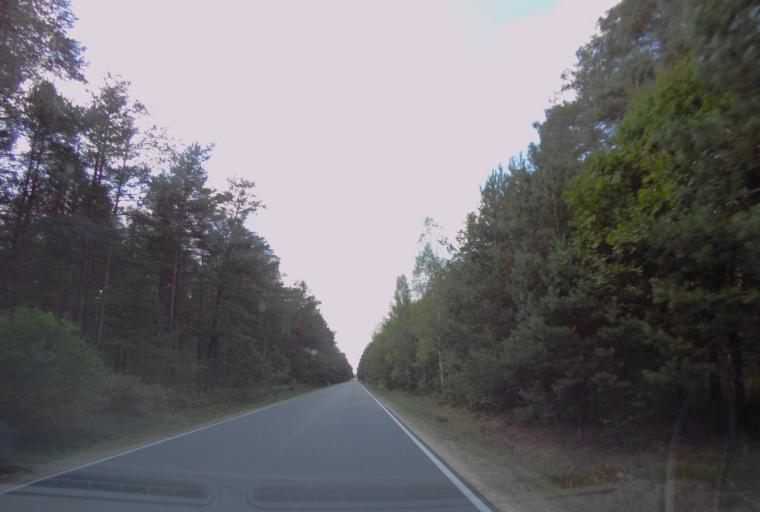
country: PL
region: Subcarpathian Voivodeship
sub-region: Powiat tarnobrzeski
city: Nowa Deba
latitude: 50.4131
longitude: 21.8407
